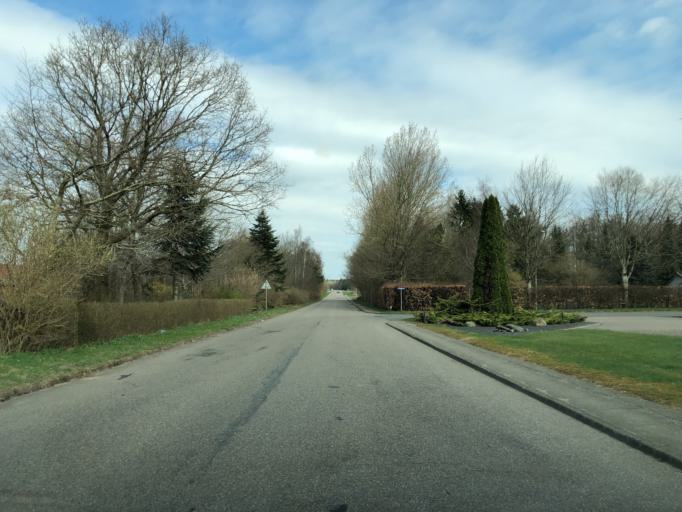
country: DK
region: South Denmark
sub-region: Vejle Kommune
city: Give
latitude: 55.9083
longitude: 9.2657
